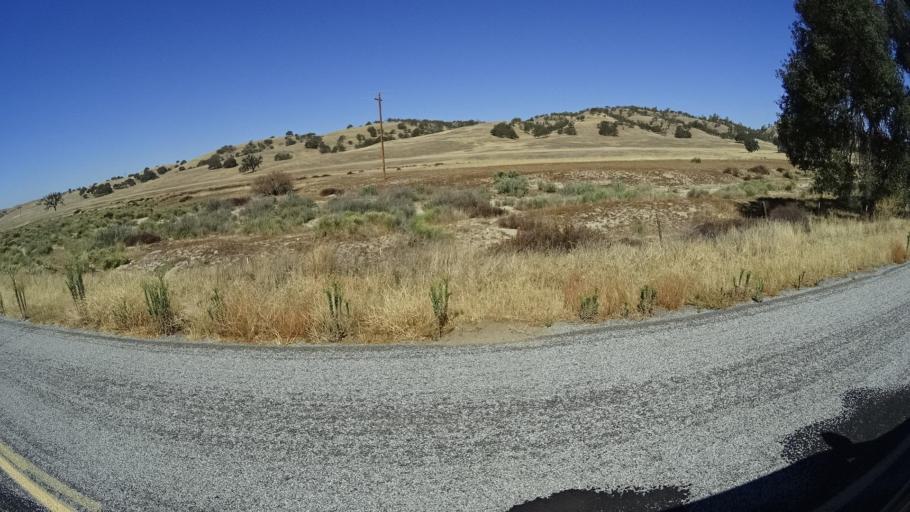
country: US
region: California
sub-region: San Luis Obispo County
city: San Miguel
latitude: 35.8283
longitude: -120.6404
